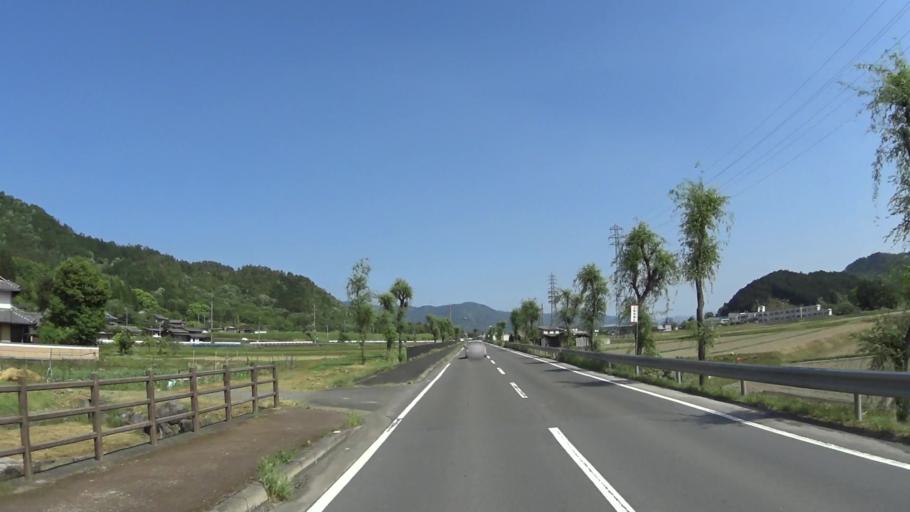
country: JP
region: Kyoto
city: Kameoka
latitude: 35.1087
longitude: 135.5212
